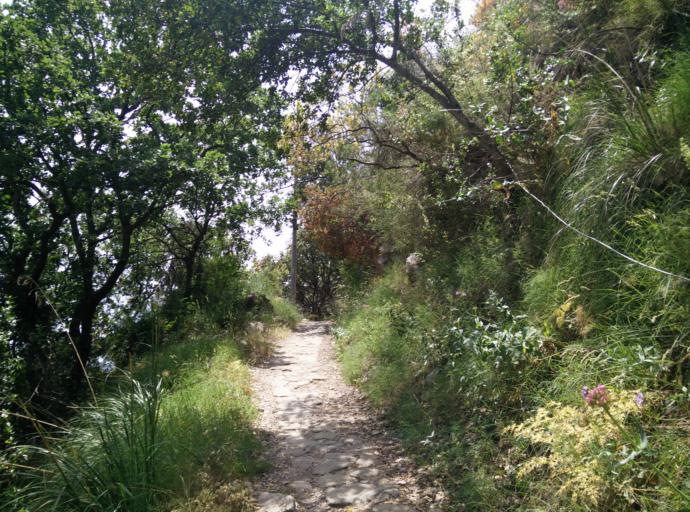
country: IT
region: Campania
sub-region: Provincia di Napoli
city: Massa Lubrense
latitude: 40.5846
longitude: 14.3478
